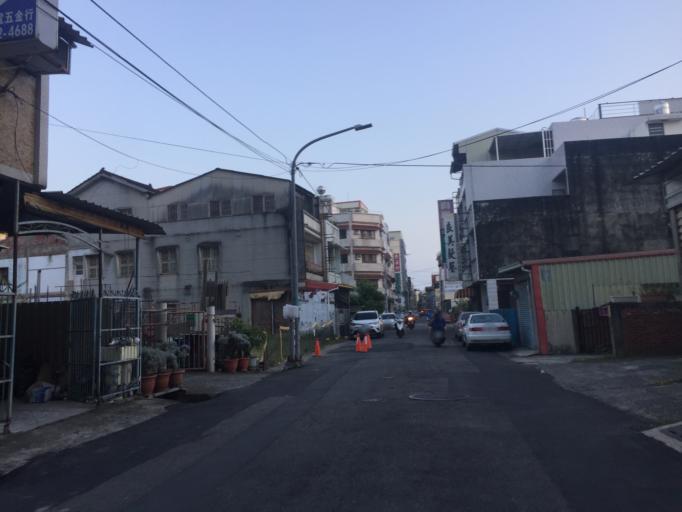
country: TW
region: Taiwan
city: Xinying
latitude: 23.3066
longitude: 120.3134
